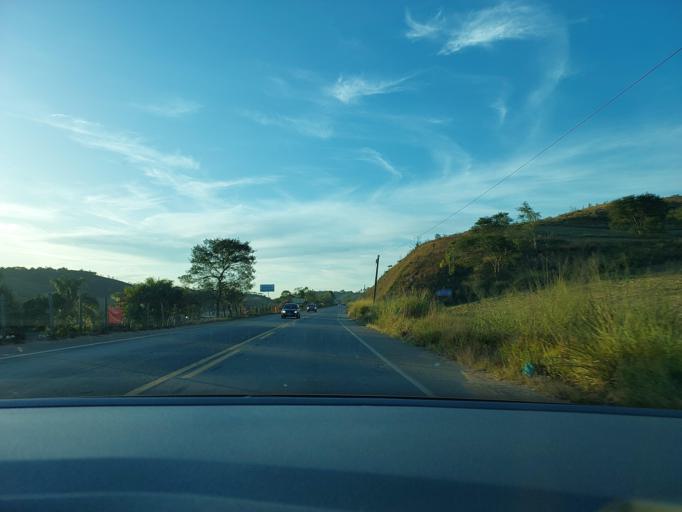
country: BR
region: Minas Gerais
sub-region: Vicosa
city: Vicosa
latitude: -20.7961
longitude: -42.8375
